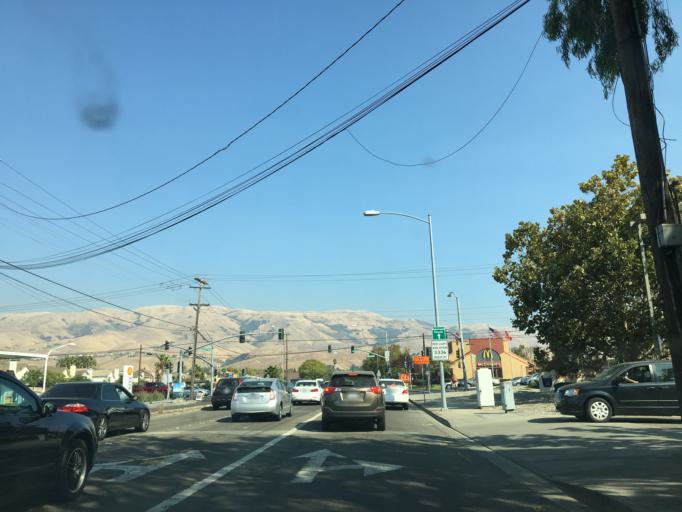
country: US
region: California
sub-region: Santa Clara County
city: Milpitas
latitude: 37.4571
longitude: -121.9124
